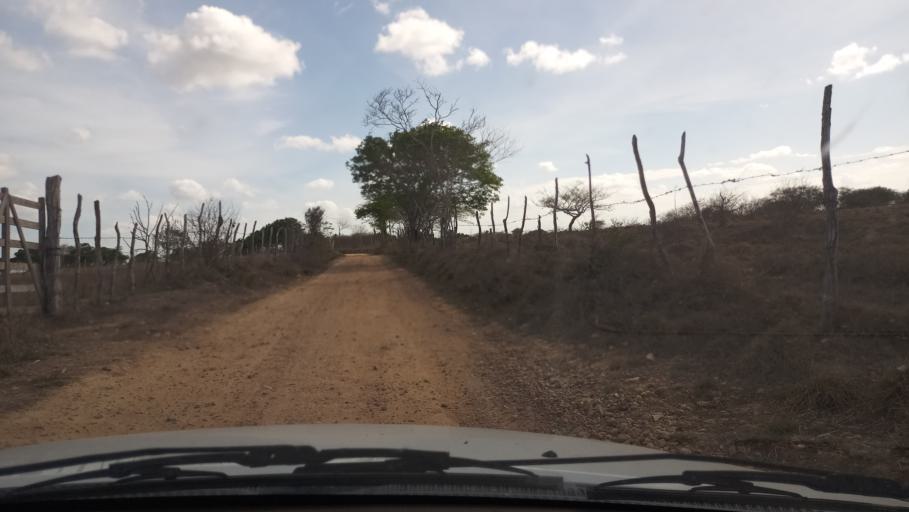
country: BR
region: Rio Grande do Norte
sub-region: Goianinha
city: Goianinha
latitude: -6.3151
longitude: -35.3074
